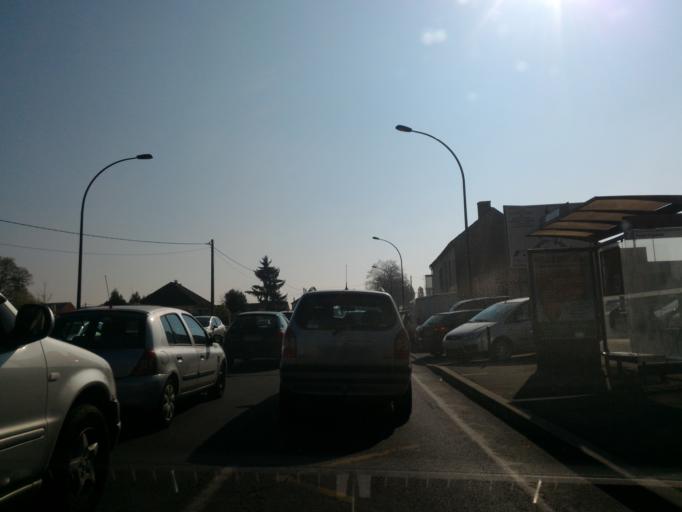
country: FR
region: Ile-de-France
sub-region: Departement du Val-de-Marne
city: La Queue-en-Brie
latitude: 48.7800
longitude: 2.5784
